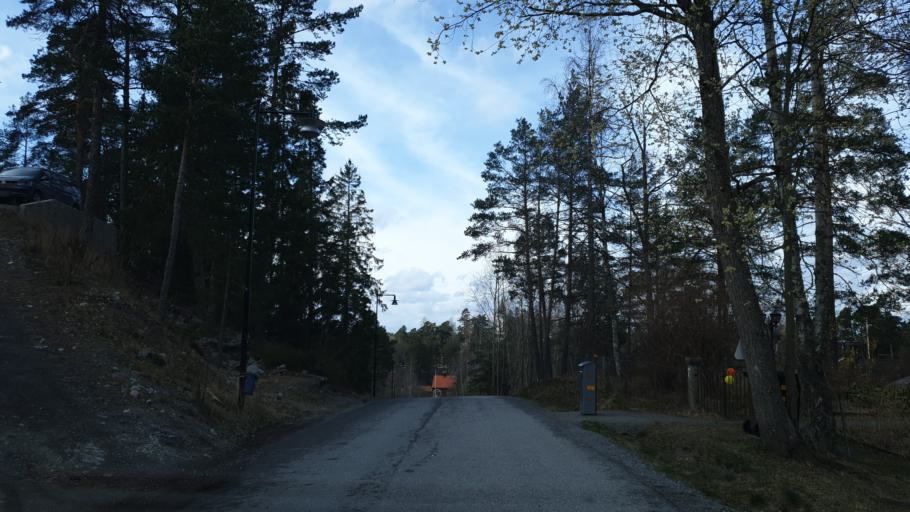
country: SE
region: Stockholm
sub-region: Nacka Kommun
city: Boo
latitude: 59.3328
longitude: 18.2953
